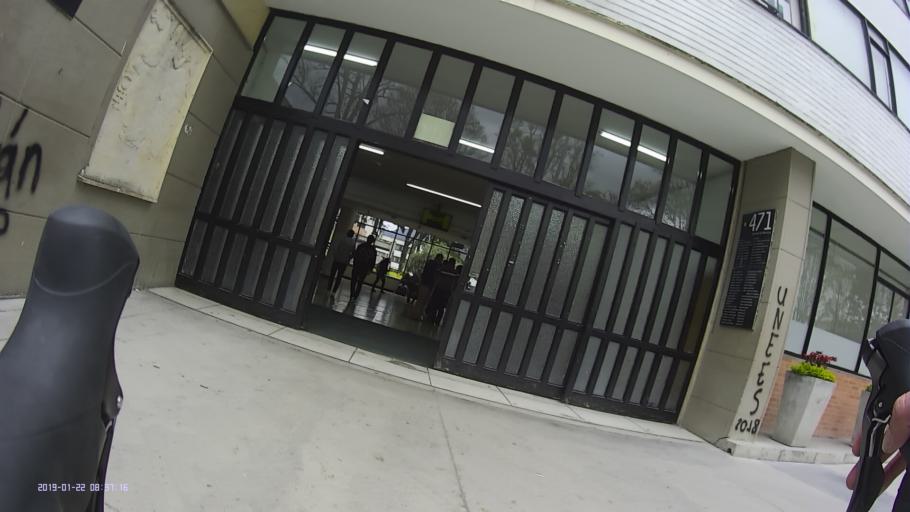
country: CO
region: Bogota D.C.
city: Bogota
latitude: 4.6365
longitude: -74.0848
